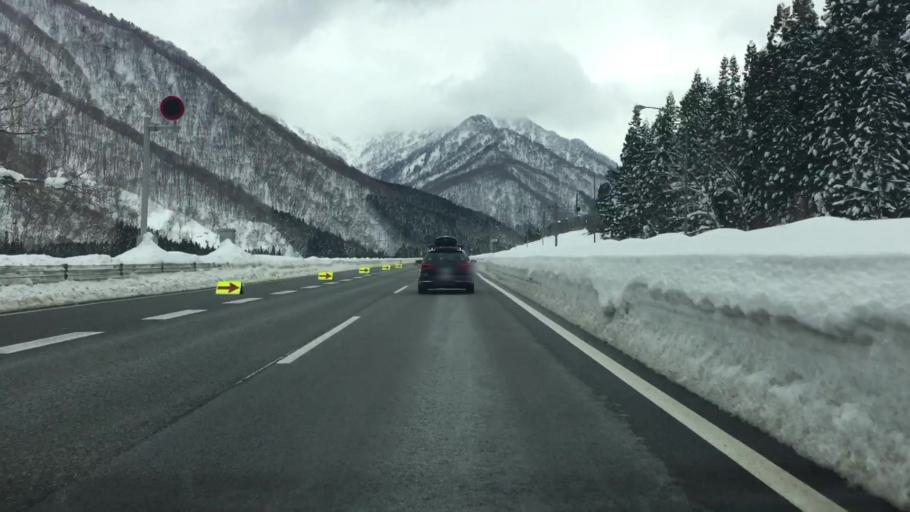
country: JP
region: Niigata
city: Shiozawa
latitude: 36.8789
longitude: 138.8574
